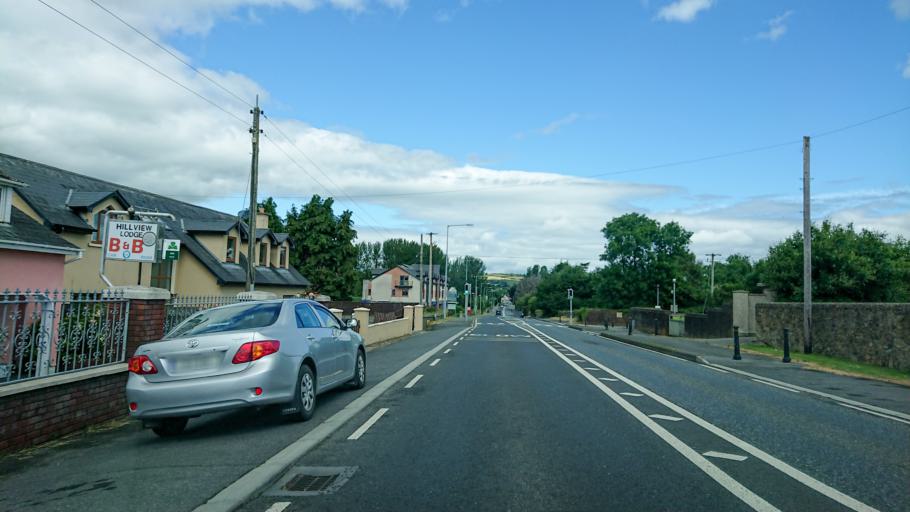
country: IE
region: Leinster
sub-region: Kilkenny
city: Mooncoin
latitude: 52.2298
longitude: -7.2384
